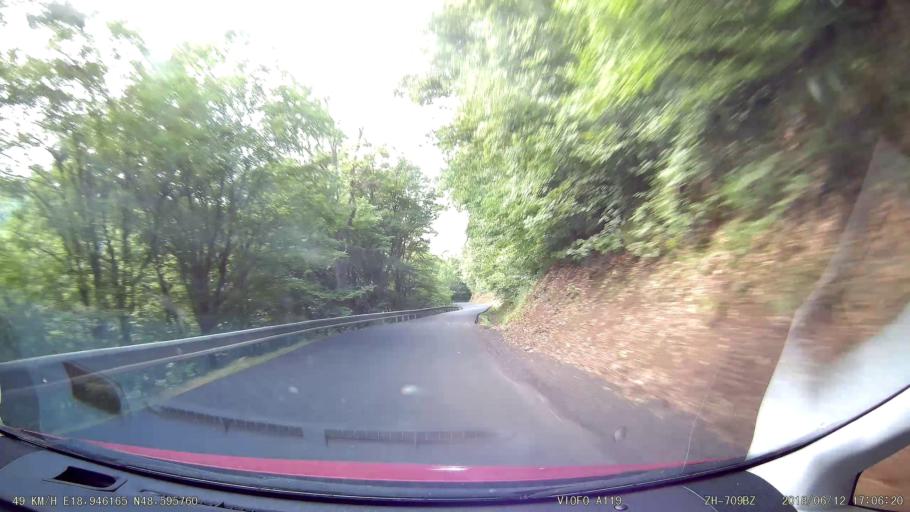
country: SK
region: Banskobystricky
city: Ziar nad Hronom
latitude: 48.5959
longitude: 18.9462
